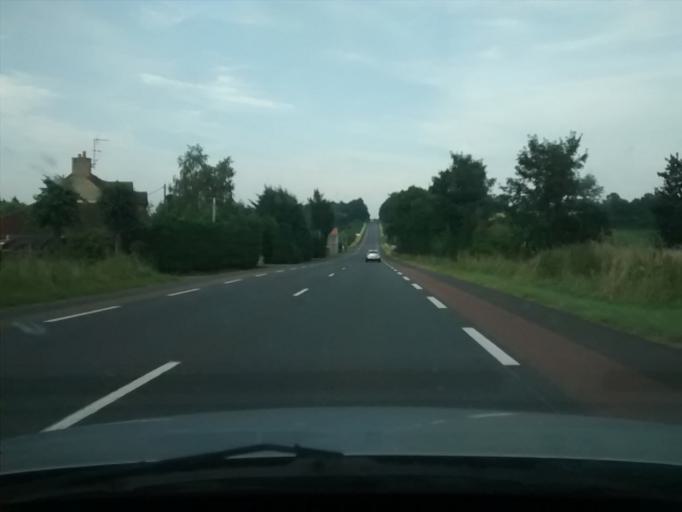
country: FR
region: Pays de la Loire
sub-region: Departement de la Sarthe
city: Coulans-sur-Gee
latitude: 48.0186
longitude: -0.0385
